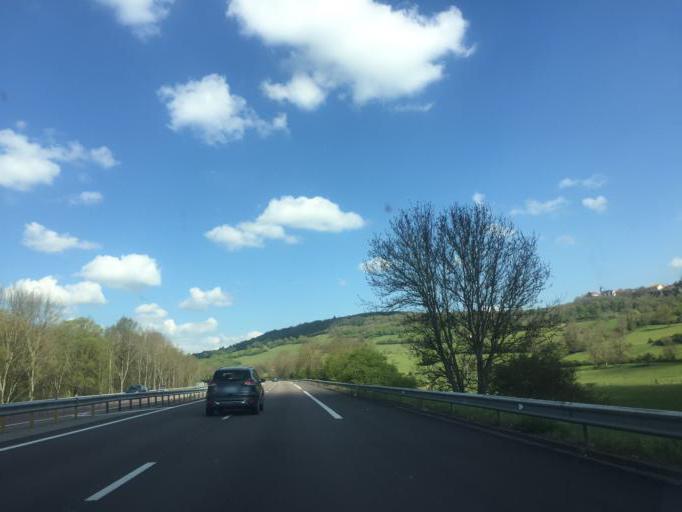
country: FR
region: Bourgogne
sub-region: Departement de la Cote-d'Or
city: Pouilly-en-Auxois
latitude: 47.1915
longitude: 4.6680
